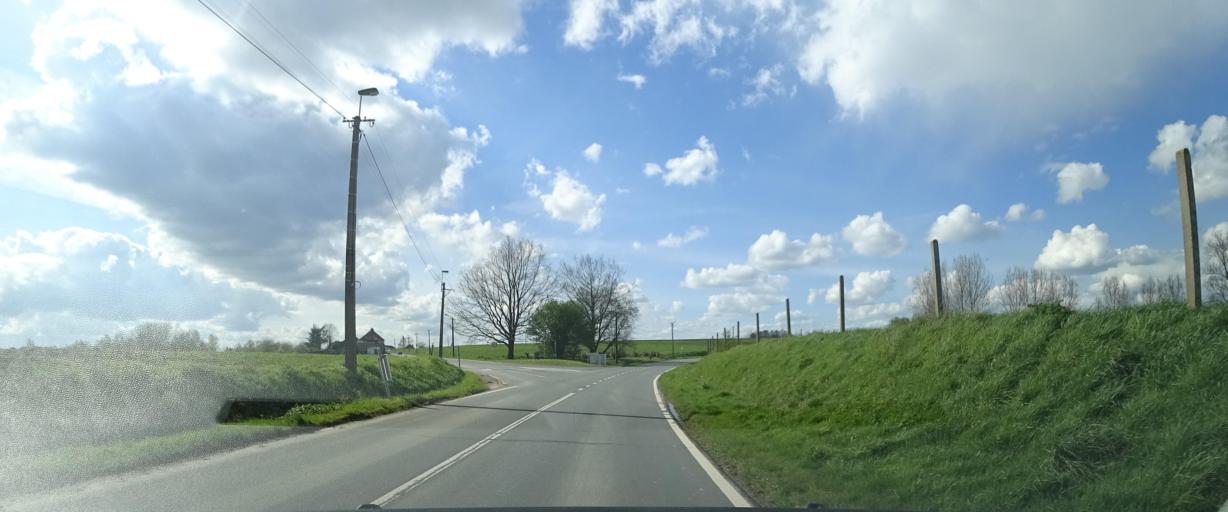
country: BE
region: Wallonia
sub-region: Province du Brabant Wallon
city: Rebecq-Rognon
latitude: 50.6503
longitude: 4.1368
